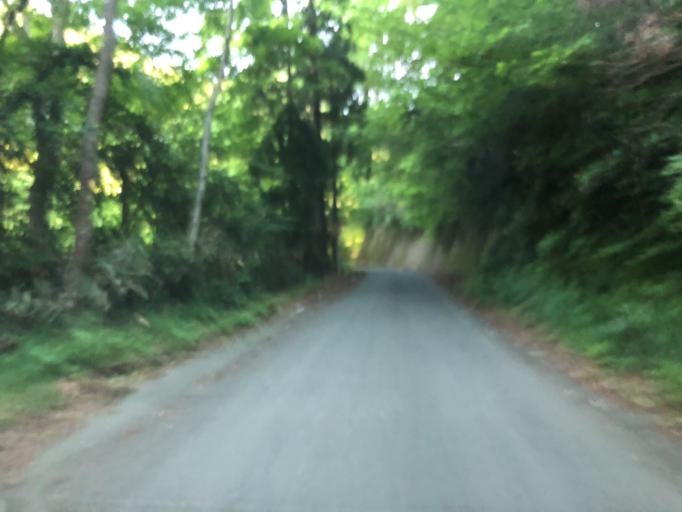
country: JP
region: Ibaraki
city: Kitaibaraki
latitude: 36.8686
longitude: 140.6975
